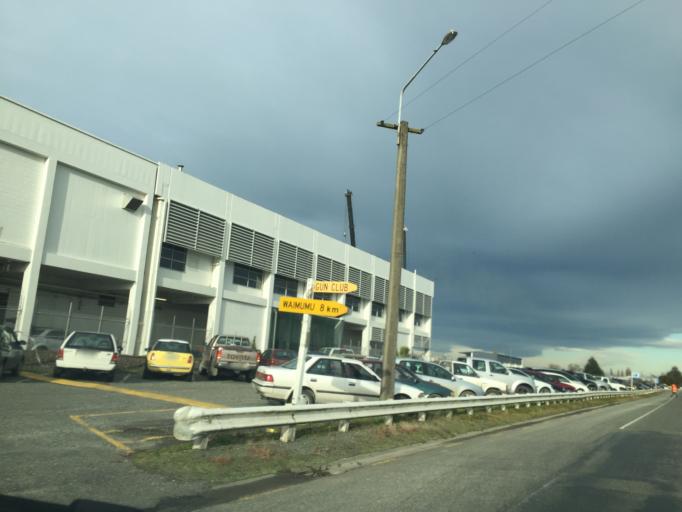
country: NZ
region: Southland
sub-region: Gore District
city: Gore
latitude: -46.1892
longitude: 168.8708
